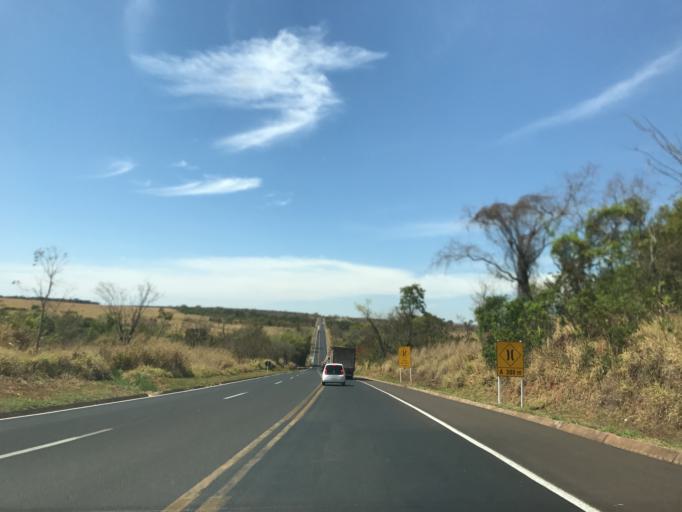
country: BR
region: Minas Gerais
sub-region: Prata
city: Prata
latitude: -19.0839
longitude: -48.9957
